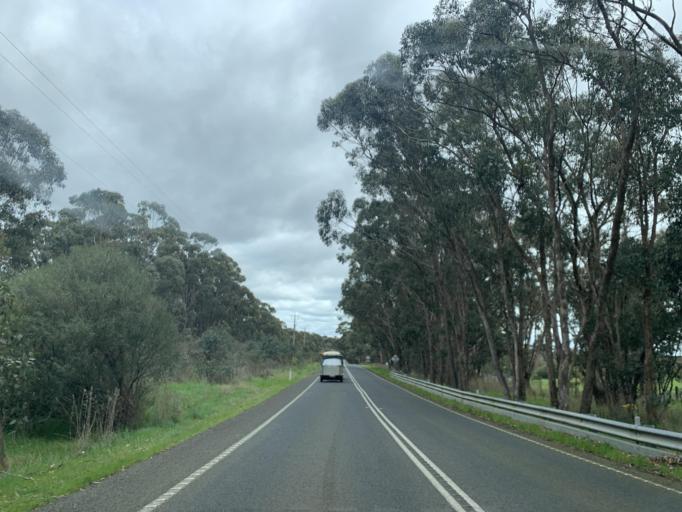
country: AU
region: Victoria
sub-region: Murrindindi
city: Kinglake West
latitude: -37.2067
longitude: 145.0783
